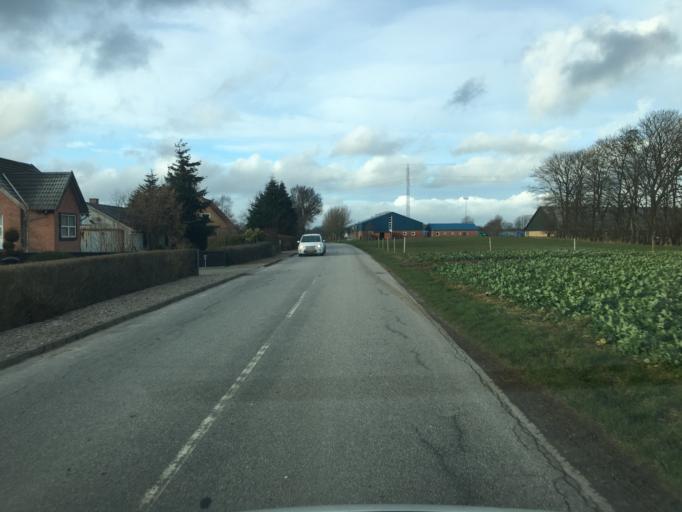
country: DK
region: South Denmark
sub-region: Sonderborg Kommune
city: Grasten
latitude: 54.9762
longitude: 9.5182
